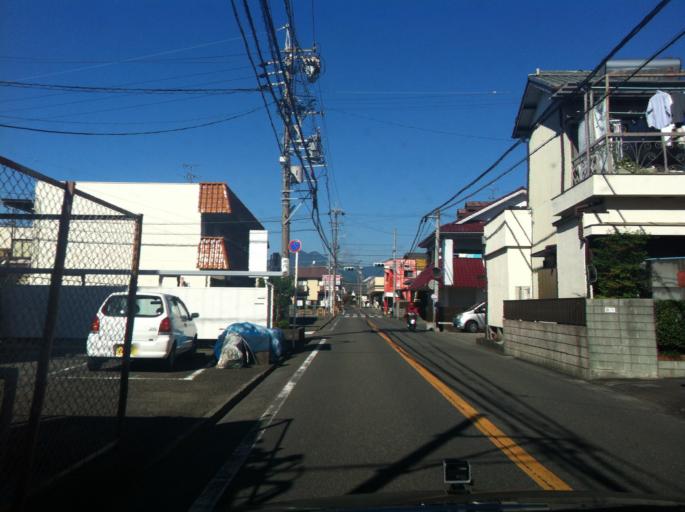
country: JP
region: Shizuoka
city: Shizuoka-shi
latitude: 34.9788
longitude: 138.4259
